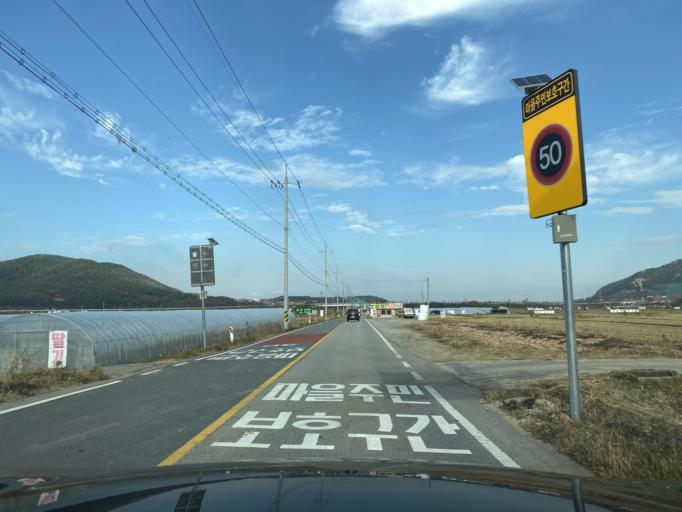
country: KR
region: Chungcheongnam-do
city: Hongsung
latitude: 36.6759
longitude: 126.6429
